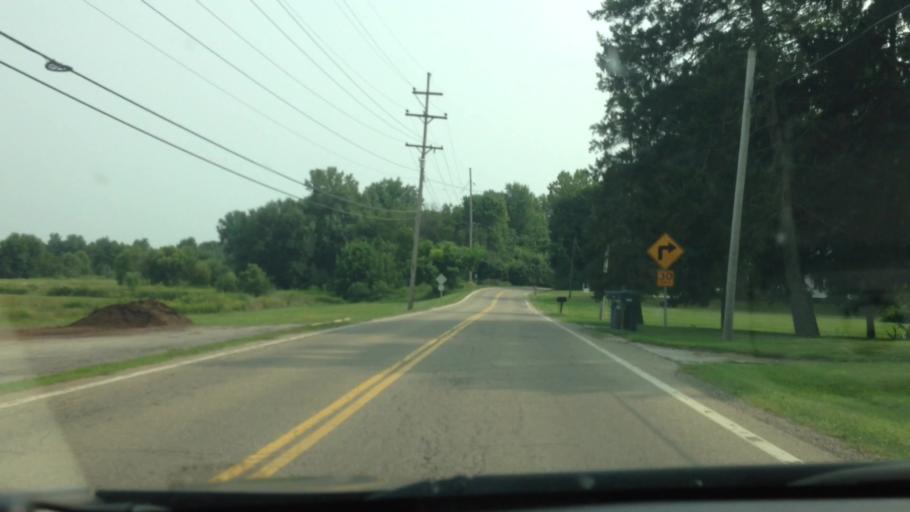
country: US
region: Ohio
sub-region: Summit County
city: Fairlawn
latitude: 41.0885
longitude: -81.5915
